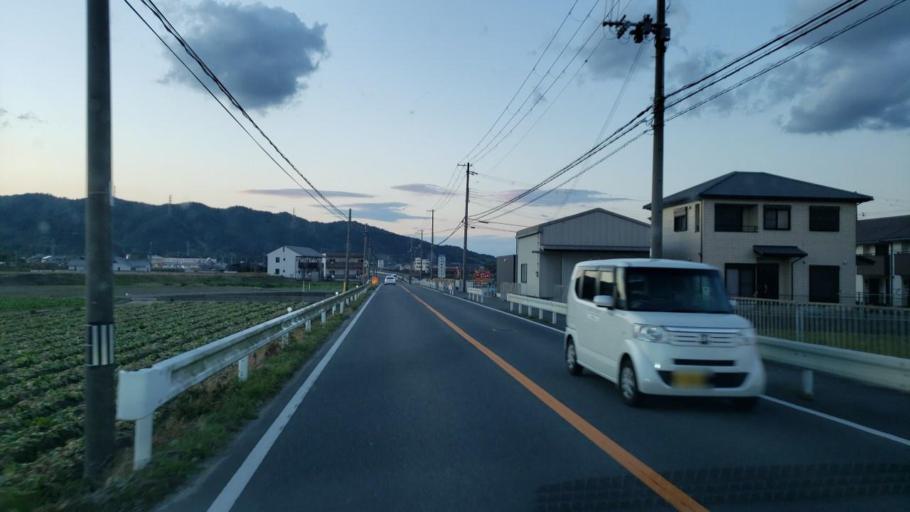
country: JP
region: Hyogo
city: Fukura
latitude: 34.3008
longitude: 134.7530
